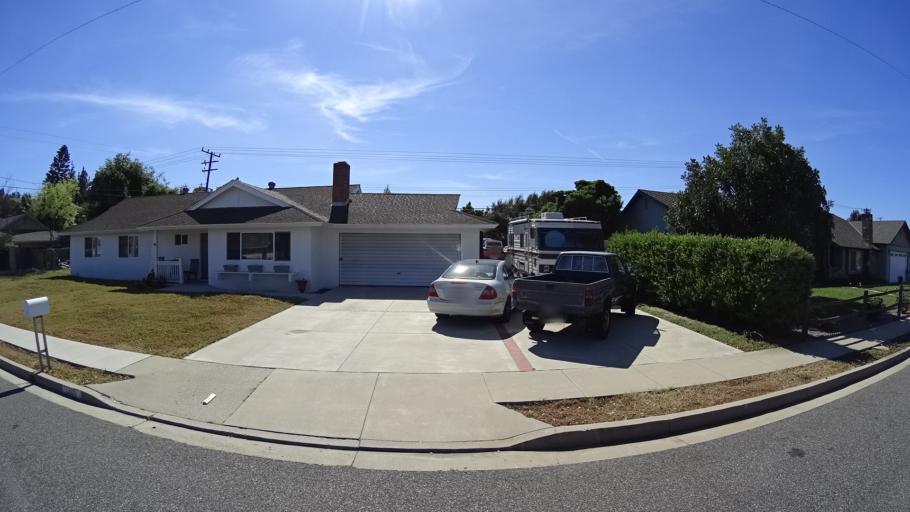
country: US
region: California
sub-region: Ventura County
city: Thousand Oaks
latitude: 34.2242
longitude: -118.8600
